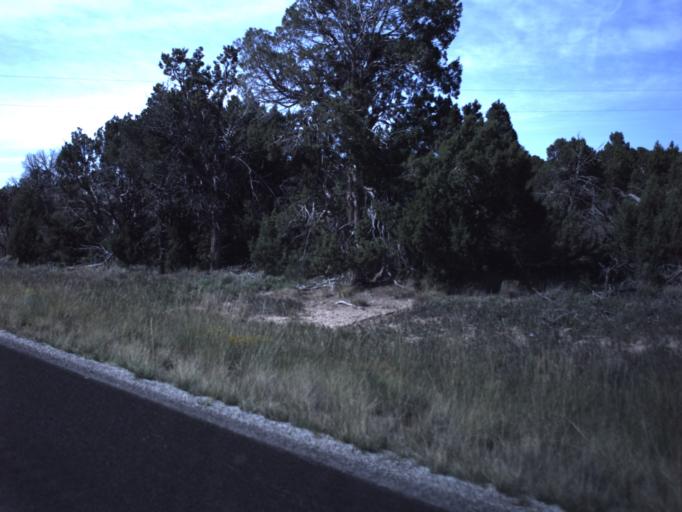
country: US
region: Utah
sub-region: San Juan County
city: Monticello
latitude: 37.8595
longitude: -109.2051
